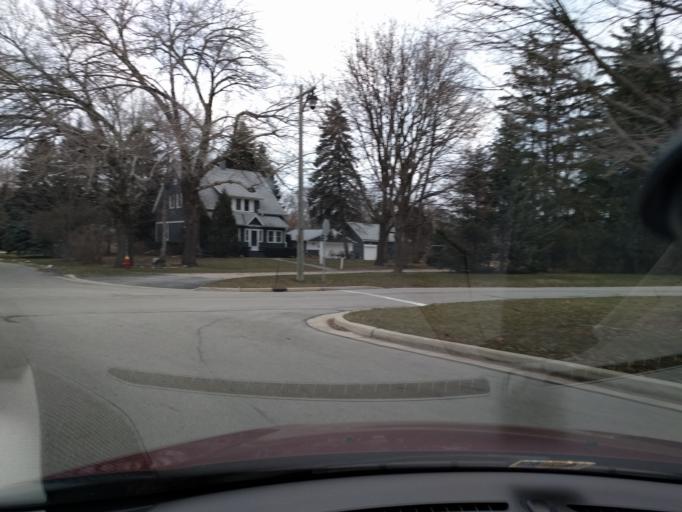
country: US
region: Wisconsin
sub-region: Milwaukee County
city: Glendale
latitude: 43.1226
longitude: -87.9264
